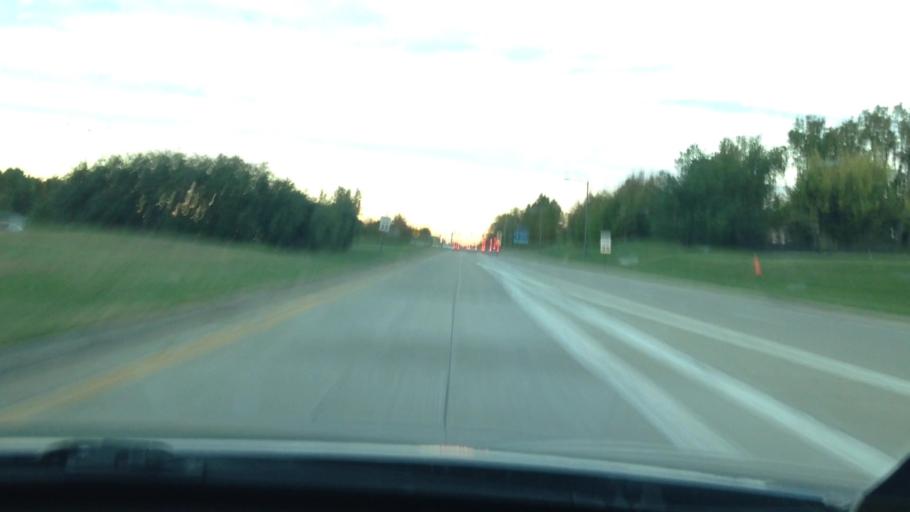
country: US
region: Missouri
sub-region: Jackson County
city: Kansas City
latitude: 39.0659
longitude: -94.5601
